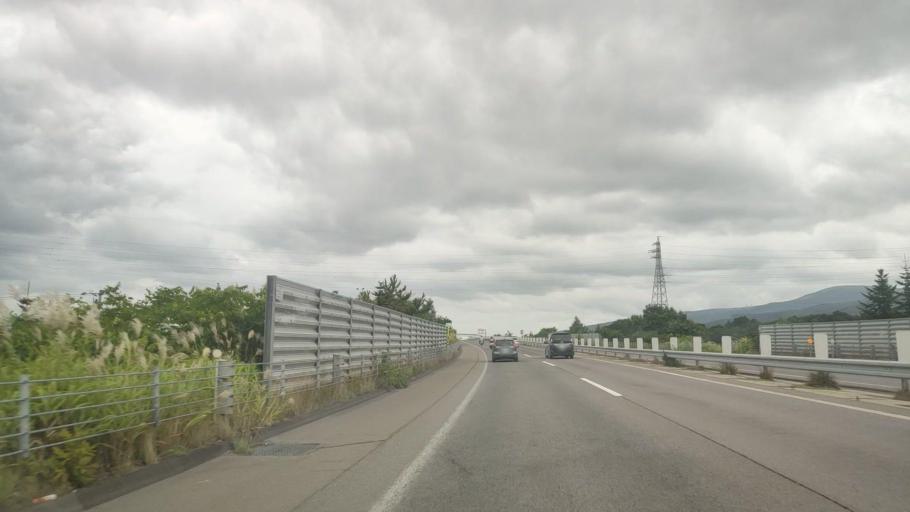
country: JP
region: Hokkaido
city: Nanae
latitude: 41.8570
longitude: 140.7368
